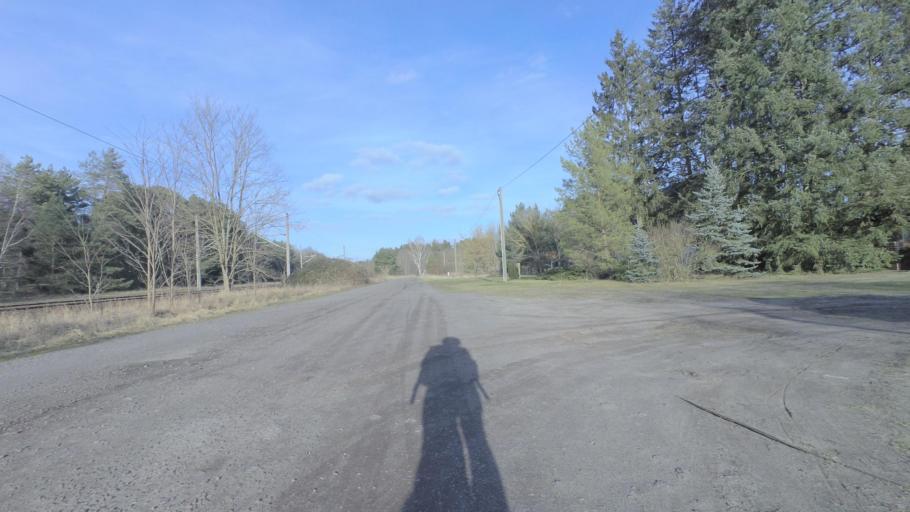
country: DE
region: Brandenburg
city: Trebbin
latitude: 52.2491
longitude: 13.2627
